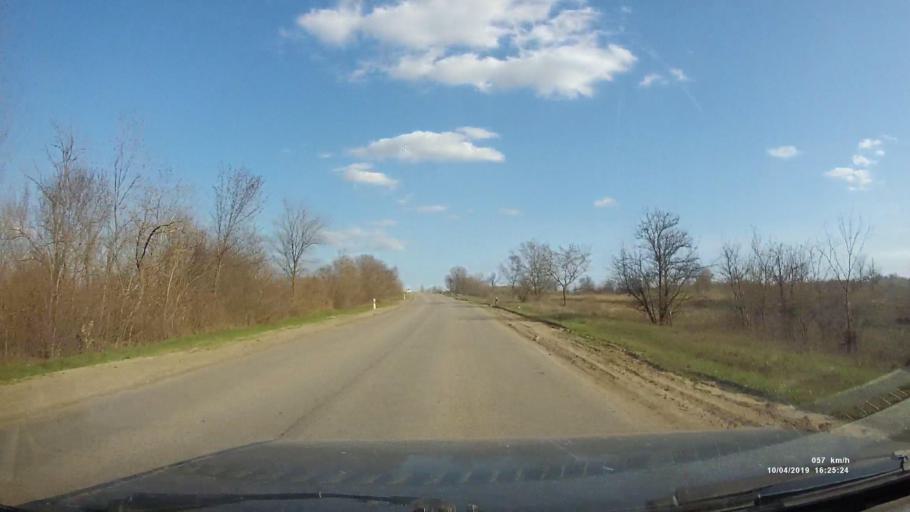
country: RU
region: Rostov
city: Staraya Stanitsa
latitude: 48.2931
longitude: 40.3232
